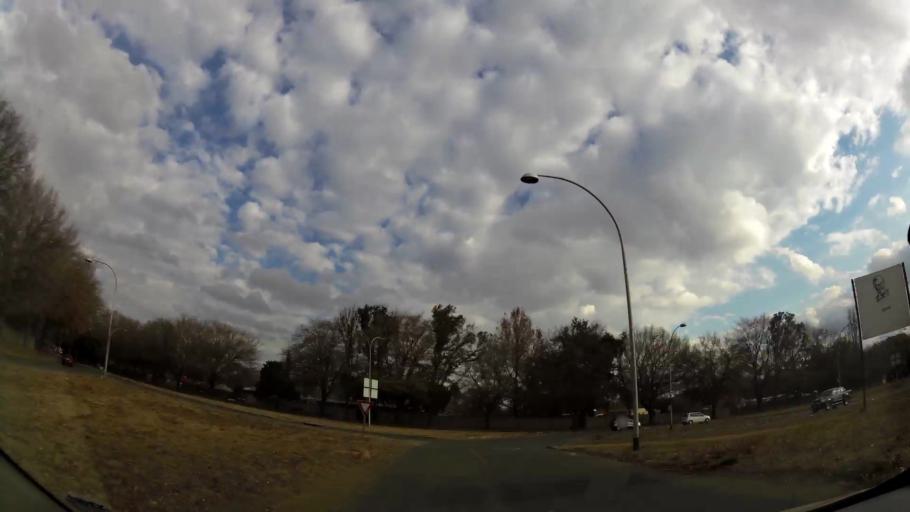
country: ZA
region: Orange Free State
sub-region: Fezile Dabi District Municipality
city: Sasolburg
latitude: -26.8042
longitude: 27.8168
